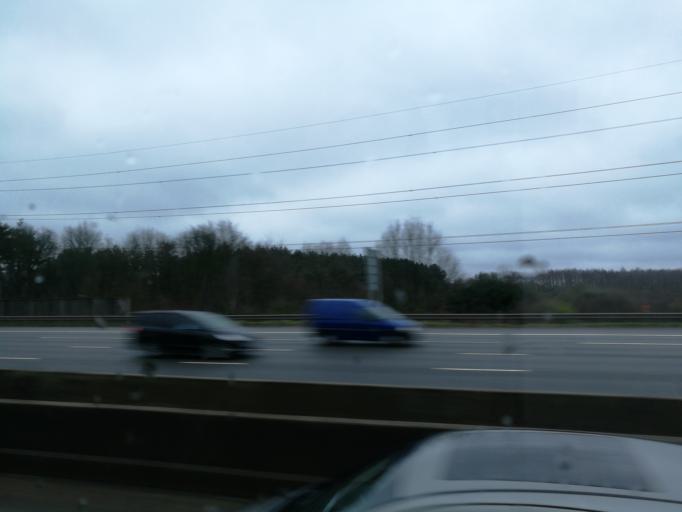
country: GB
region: England
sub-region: Hertfordshire
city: Abbots Langley
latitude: 51.7392
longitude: -0.3954
